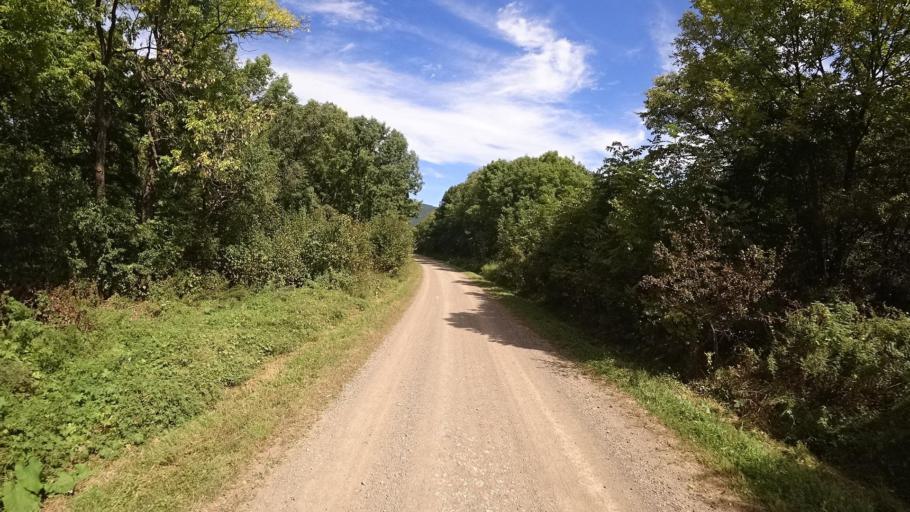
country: RU
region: Primorskiy
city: Yakovlevka
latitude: 44.6589
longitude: 133.7471
